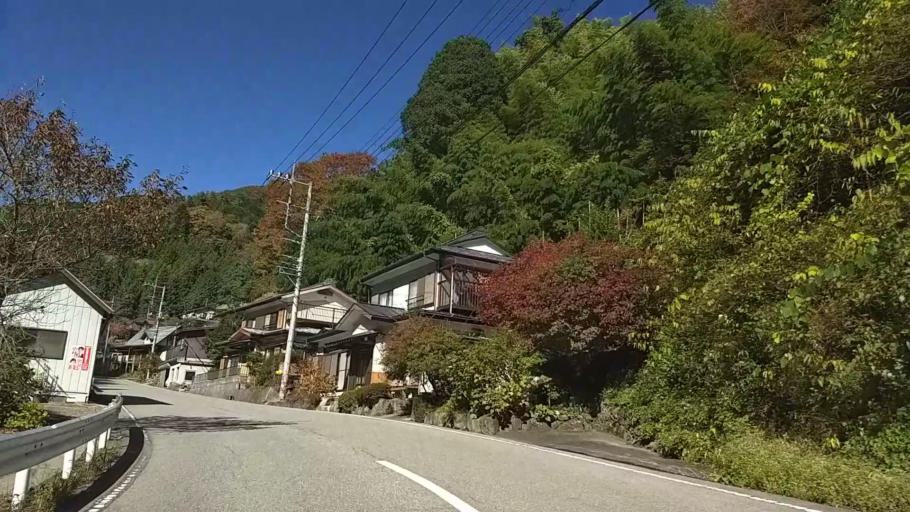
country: JP
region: Yamanashi
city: Uenohara
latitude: 35.6950
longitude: 139.0403
